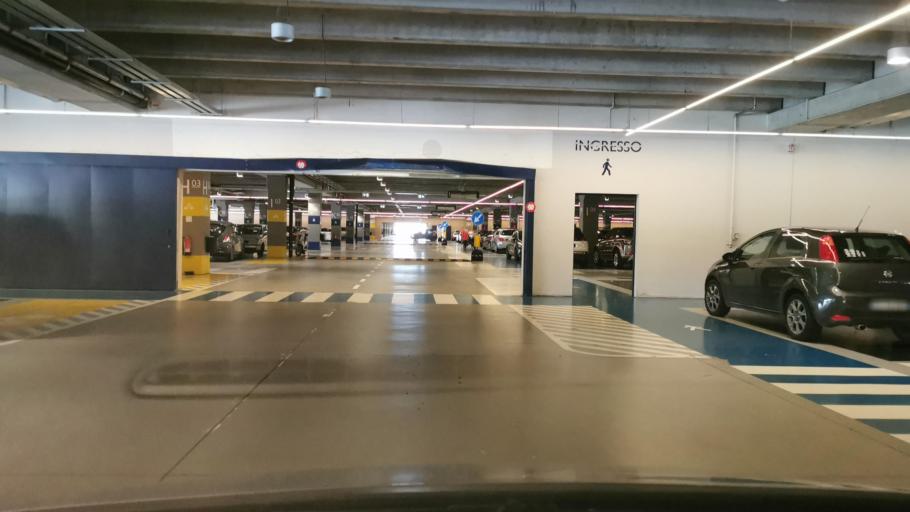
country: IT
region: Piedmont
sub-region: Provincia di Torino
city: Settimo Torinese
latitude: 45.1282
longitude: 7.7372
